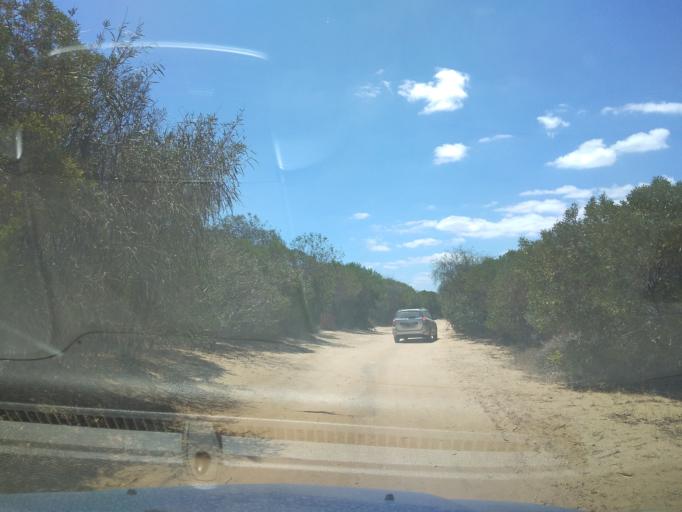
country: TN
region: Susah
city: Harqalah
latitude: 36.1609
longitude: 10.4639
